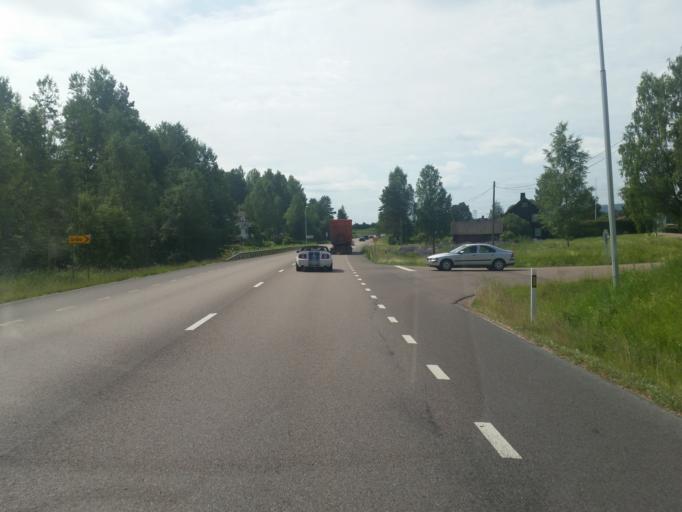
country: SE
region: Dalarna
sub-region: Gagnefs Kommun
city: Gagnef
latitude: 60.6224
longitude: 15.0558
